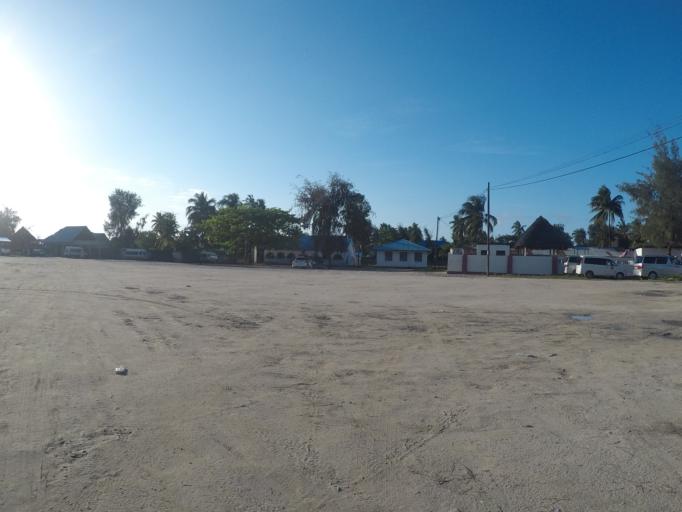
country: TZ
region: Zanzibar North
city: Nungwi
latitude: -5.7281
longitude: 39.2934
